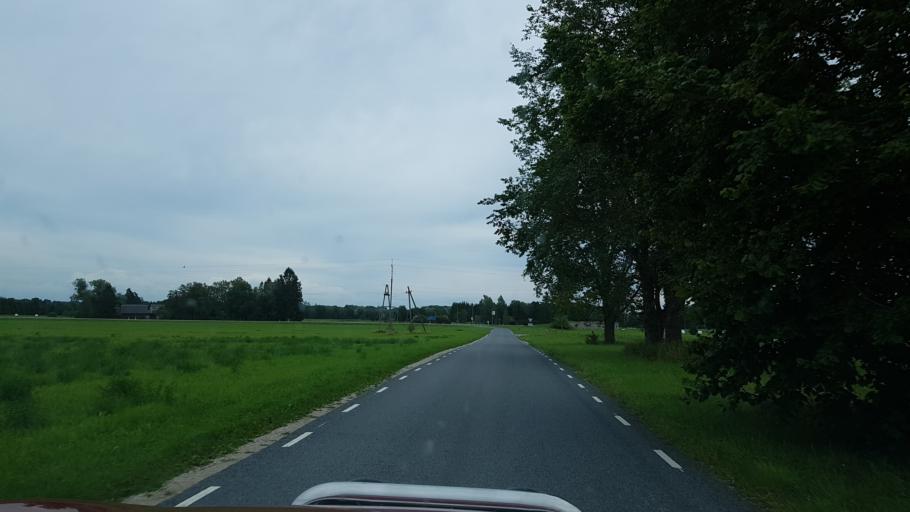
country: EE
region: Harju
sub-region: Nissi vald
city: Turba
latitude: 58.8765
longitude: 24.0821
